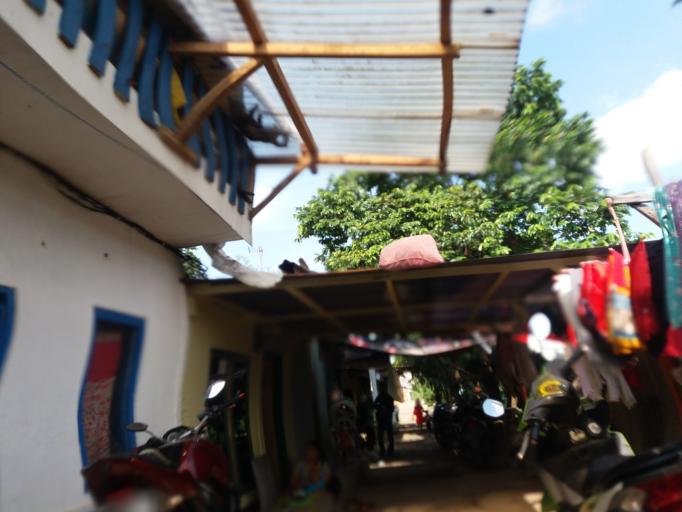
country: ID
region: West Java
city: Bandung
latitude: -6.9302
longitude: 107.6657
